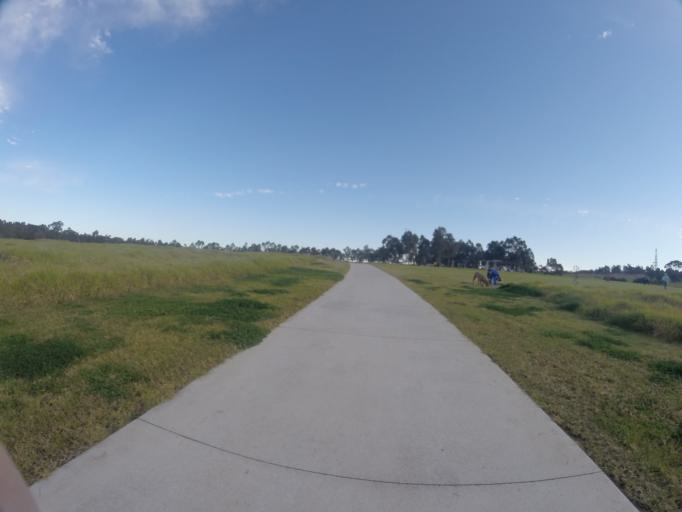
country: AU
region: New South Wales
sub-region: Fairfield
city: Horsley Park
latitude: -33.8604
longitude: 150.8693
